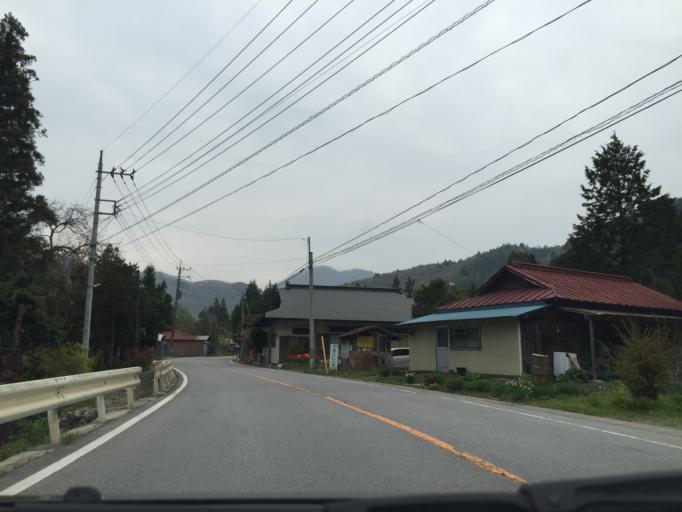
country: JP
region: Tochigi
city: Nikko
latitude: 36.9755
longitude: 139.6904
